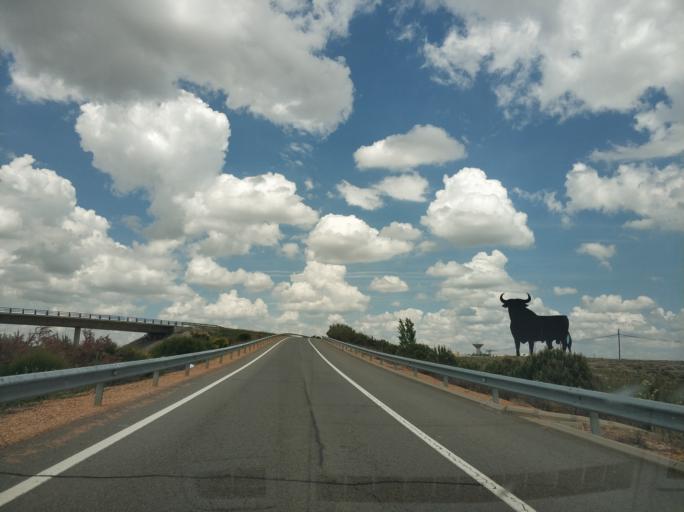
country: ES
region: Castille and Leon
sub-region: Provincia de Salamanca
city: Carbajosa de la Sagrada
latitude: 40.9221
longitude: -5.6673
